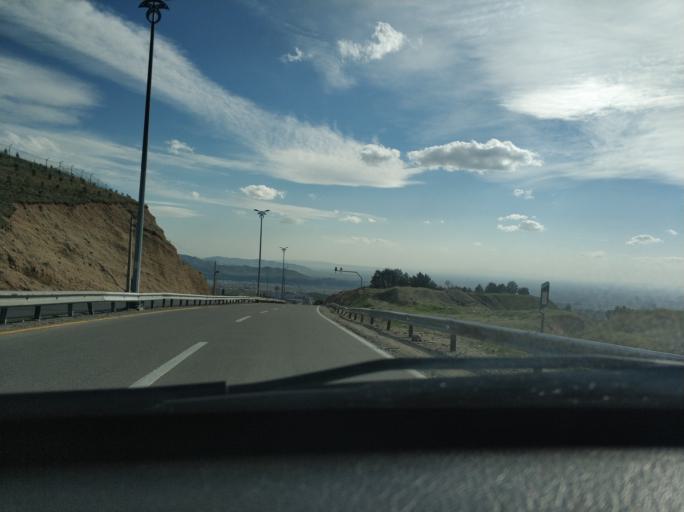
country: IR
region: Tehran
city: Tajrish
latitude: 35.7883
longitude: 51.5669
